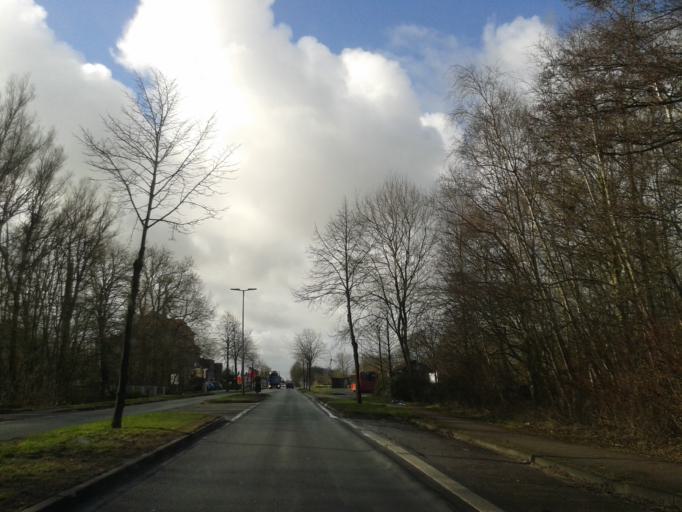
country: DE
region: Lower Saxony
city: Upgant-Schott
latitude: 53.4744
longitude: 7.3223
